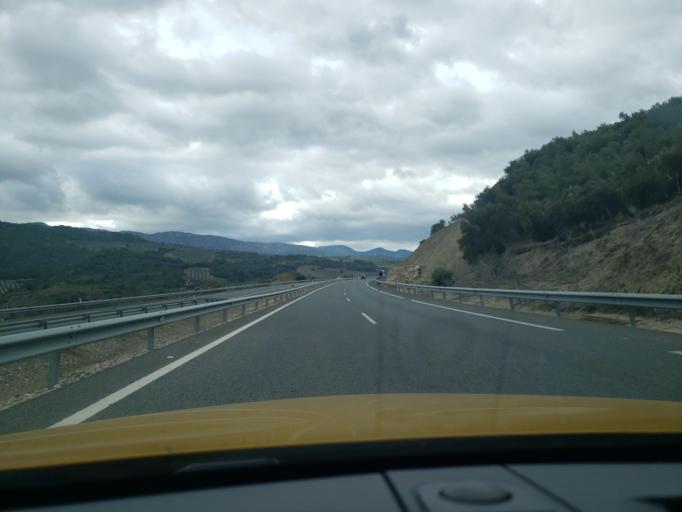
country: ES
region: Andalusia
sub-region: Provincia de Jaen
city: Pegalajar
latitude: 37.7178
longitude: -3.6587
